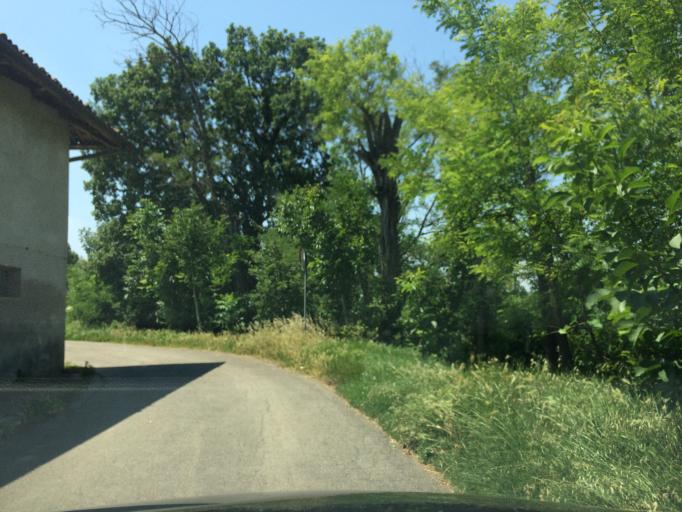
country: IT
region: Piedmont
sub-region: Provincia di Asti
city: Moasca
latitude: 44.7662
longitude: 8.2653
